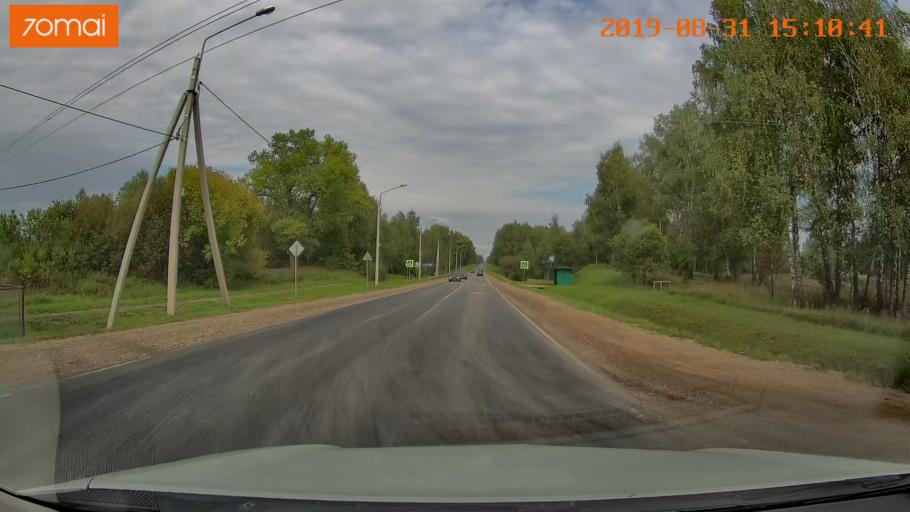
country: RU
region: Kaluga
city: Spas-Demensk
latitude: 54.4162
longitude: 34.2256
